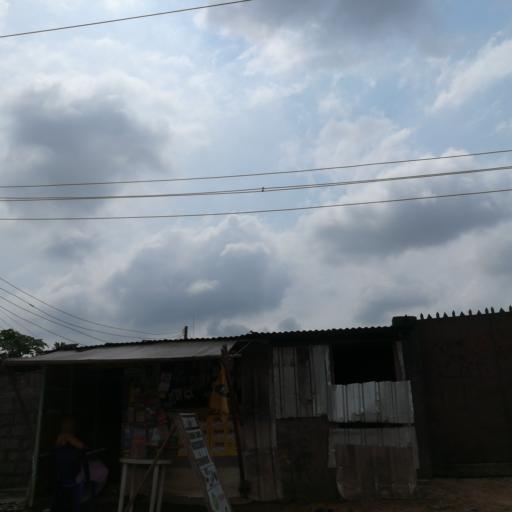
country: NG
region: Rivers
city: Port Harcourt
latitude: 4.8422
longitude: 7.0694
